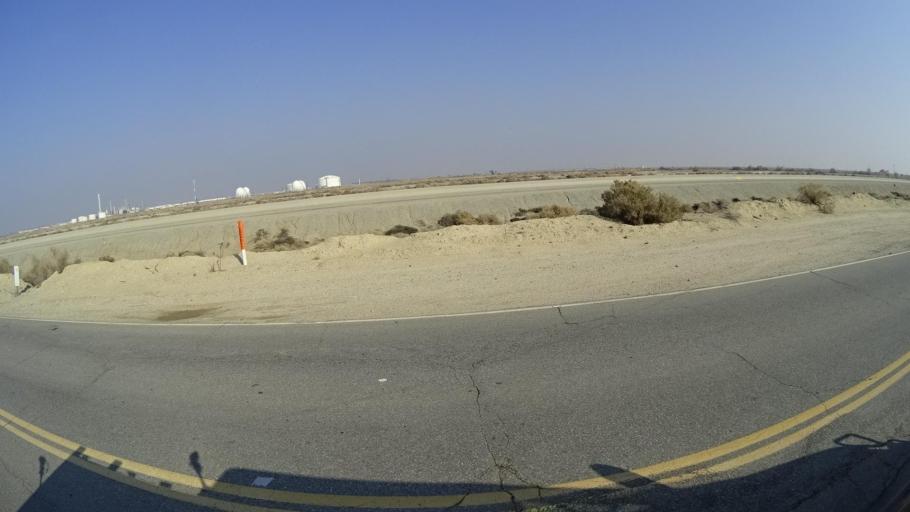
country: US
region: California
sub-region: Kern County
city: Ford City
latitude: 35.2697
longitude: -119.3126
